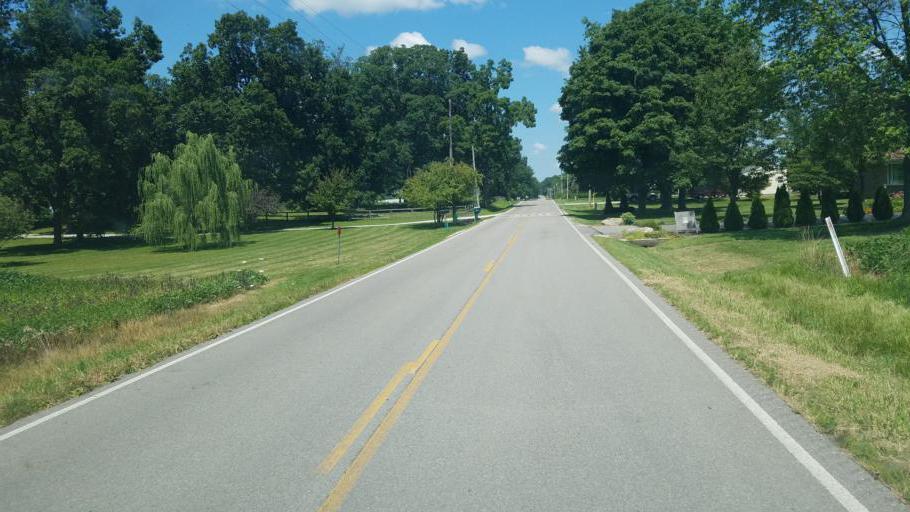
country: US
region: Ohio
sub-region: Marion County
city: Marion
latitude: 40.6512
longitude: -83.1733
